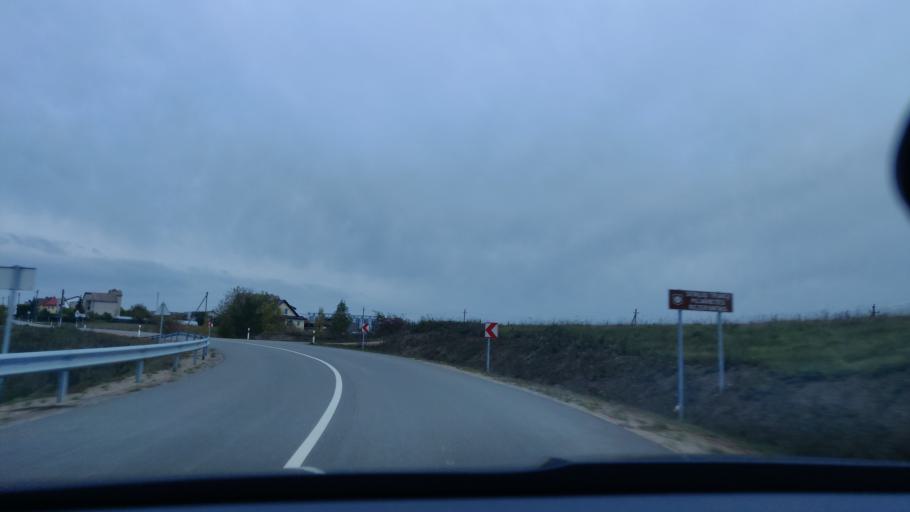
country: LT
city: Trakai
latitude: 54.6092
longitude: 24.9927
